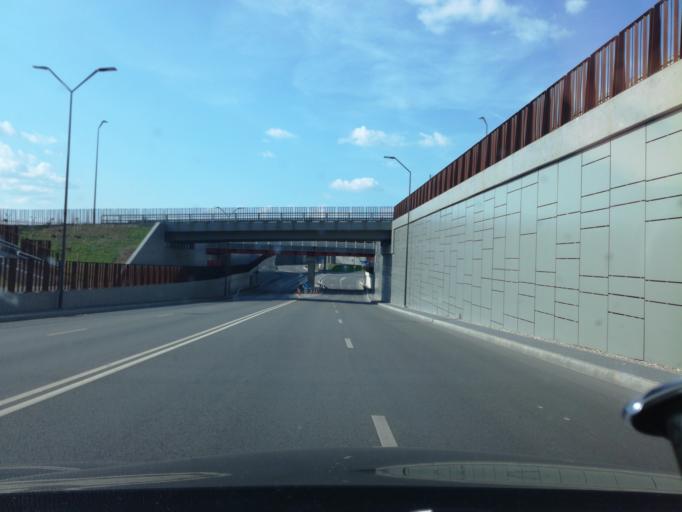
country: LT
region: Marijampoles apskritis
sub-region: Marijampole Municipality
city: Marijampole
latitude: 54.5374
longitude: 23.3514
